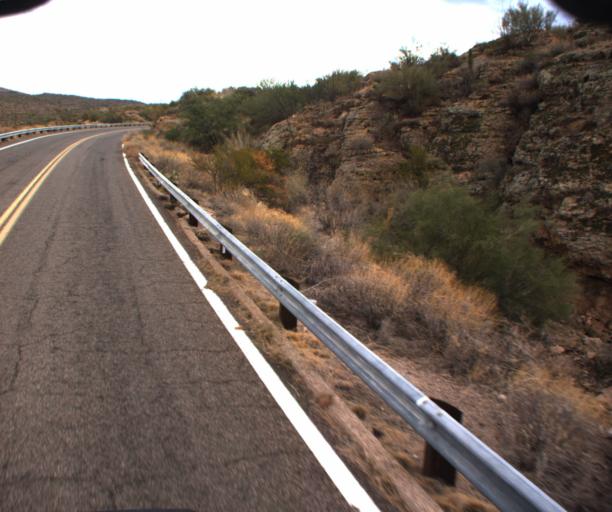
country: US
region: Arizona
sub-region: Pinal County
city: Apache Junction
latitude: 33.5330
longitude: -111.3633
